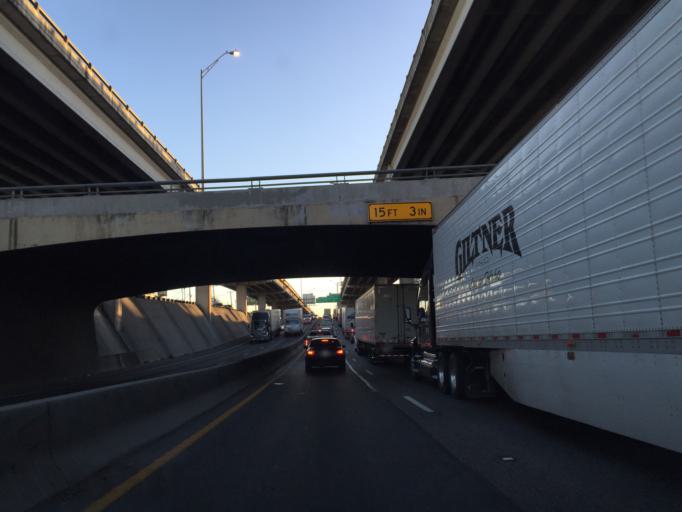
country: US
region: Texas
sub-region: Travis County
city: Austin
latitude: 30.2950
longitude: -97.7195
